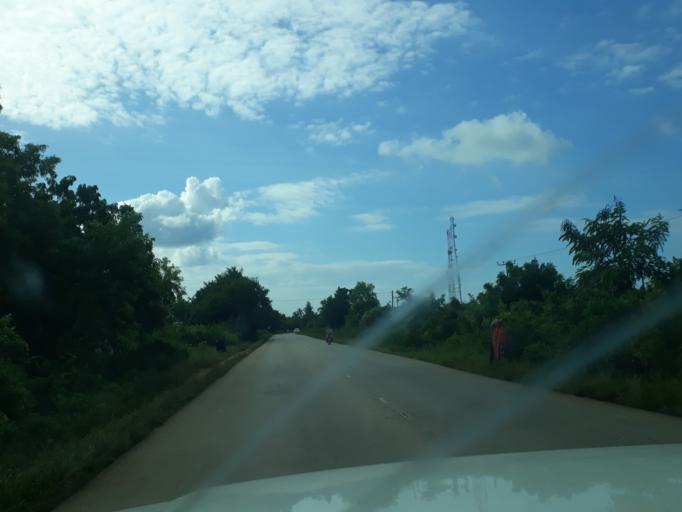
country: TZ
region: Zanzibar North
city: Nungwi
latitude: -5.7670
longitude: 39.3014
